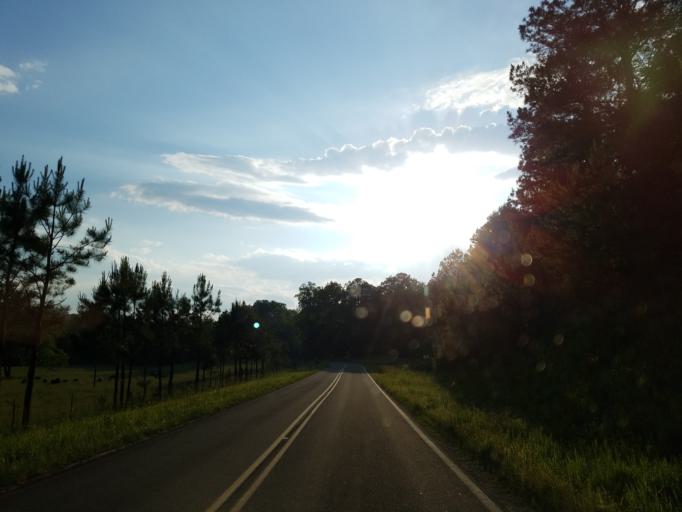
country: US
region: Georgia
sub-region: Cherokee County
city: Ball Ground
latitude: 34.2995
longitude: -84.3797
